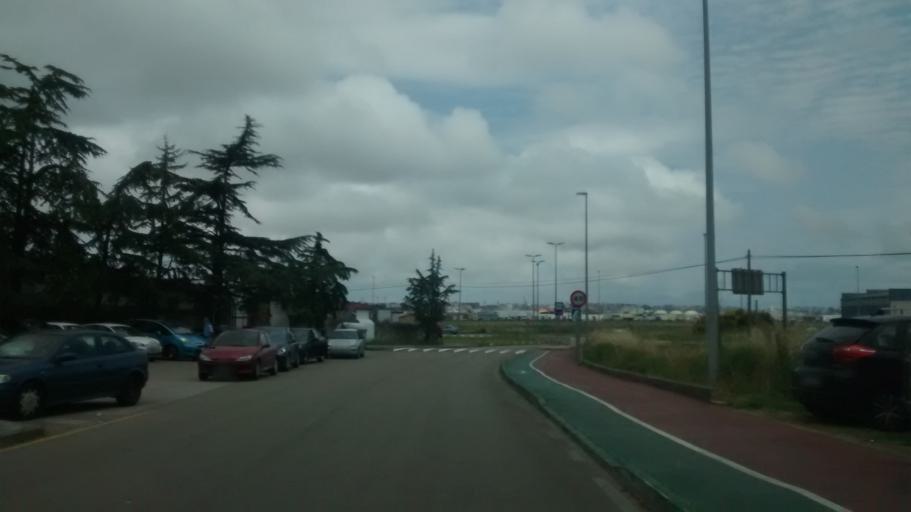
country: ES
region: Cantabria
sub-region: Provincia de Cantabria
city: El Astillero
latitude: 43.4231
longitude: -3.8285
